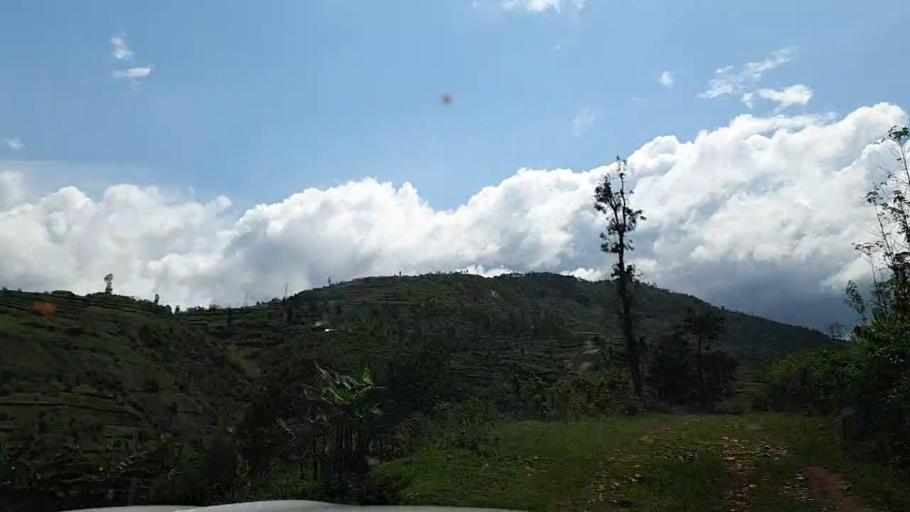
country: RW
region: Southern Province
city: Gikongoro
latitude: -2.3608
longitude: 29.5390
